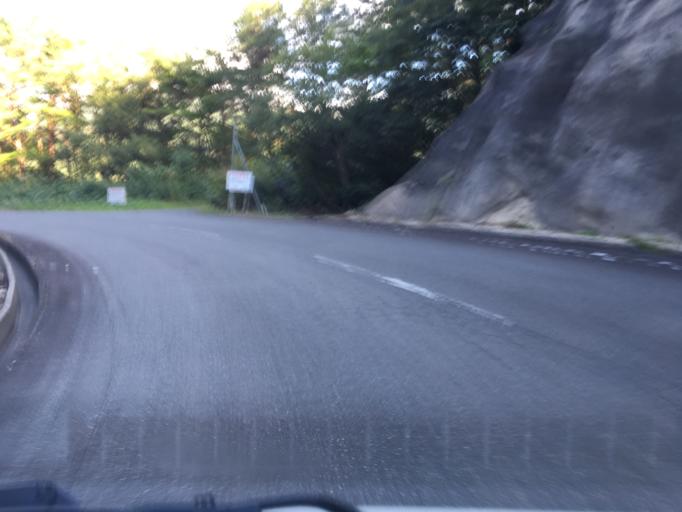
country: JP
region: Yamagata
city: Yonezawa
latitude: 37.8701
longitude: 140.1878
